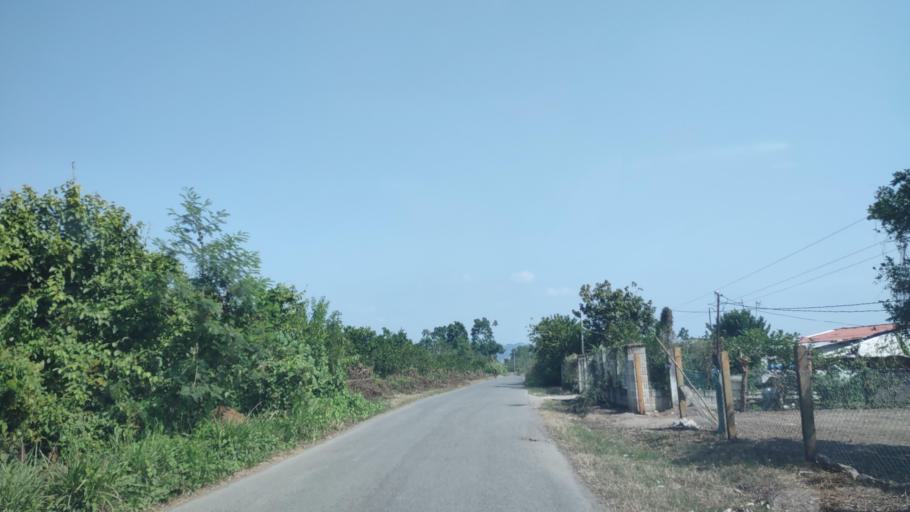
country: MX
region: Puebla
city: Espinal
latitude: 20.2579
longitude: -97.3215
